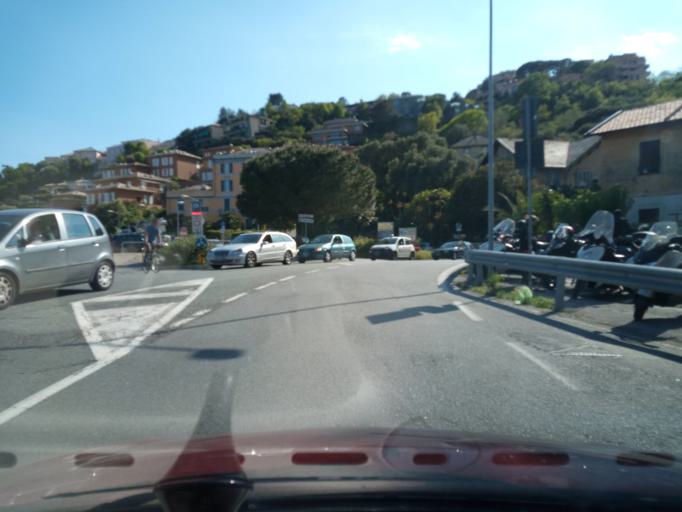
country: IT
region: Liguria
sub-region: Provincia di Genova
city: Arenzano
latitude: 44.4007
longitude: 8.6853
